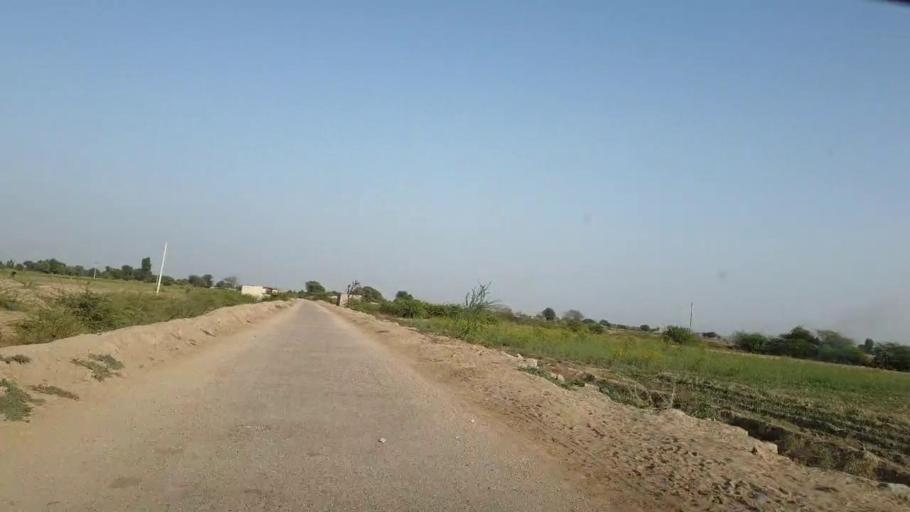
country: PK
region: Sindh
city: Kunri
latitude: 25.0779
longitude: 69.4420
